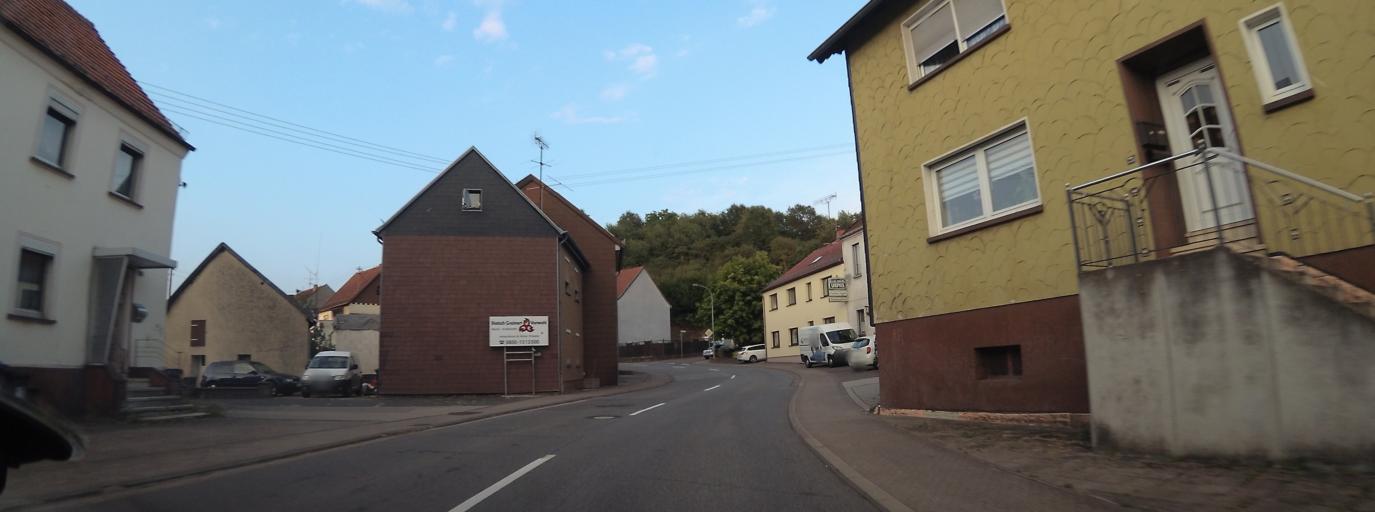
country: DE
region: Saarland
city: Tholey
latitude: 49.5315
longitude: 6.9736
